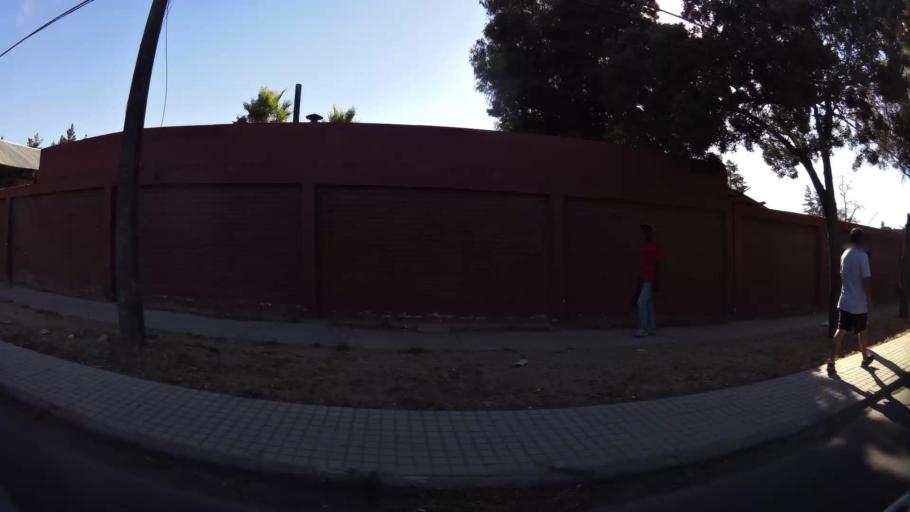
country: CL
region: O'Higgins
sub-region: Provincia de Colchagua
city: Chimbarongo
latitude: -34.5916
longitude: -70.9746
